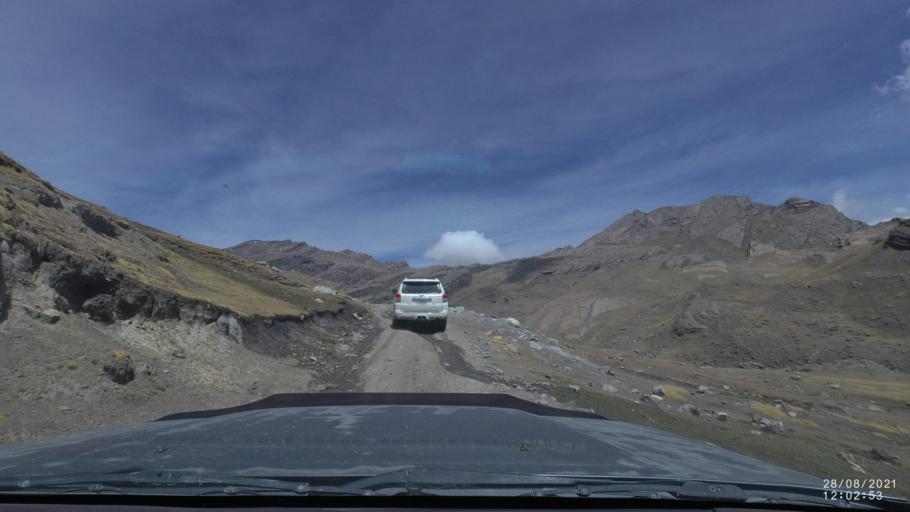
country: BO
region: Cochabamba
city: Sipe Sipe
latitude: -17.2632
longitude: -66.3838
